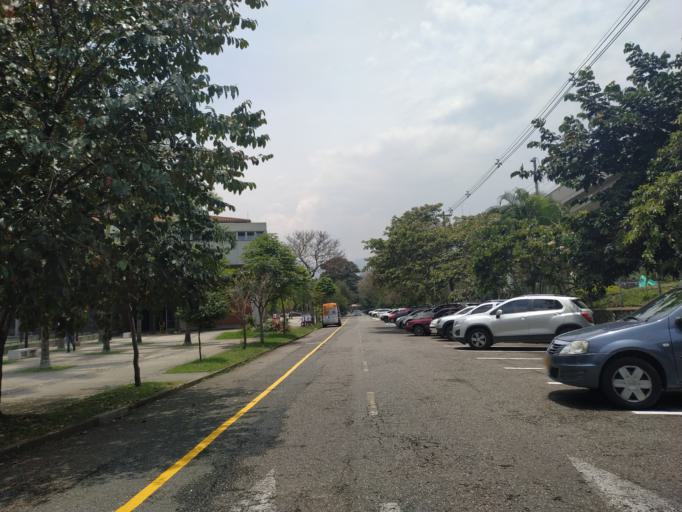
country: CO
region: Antioquia
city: Medellin
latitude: 6.2697
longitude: -75.5674
